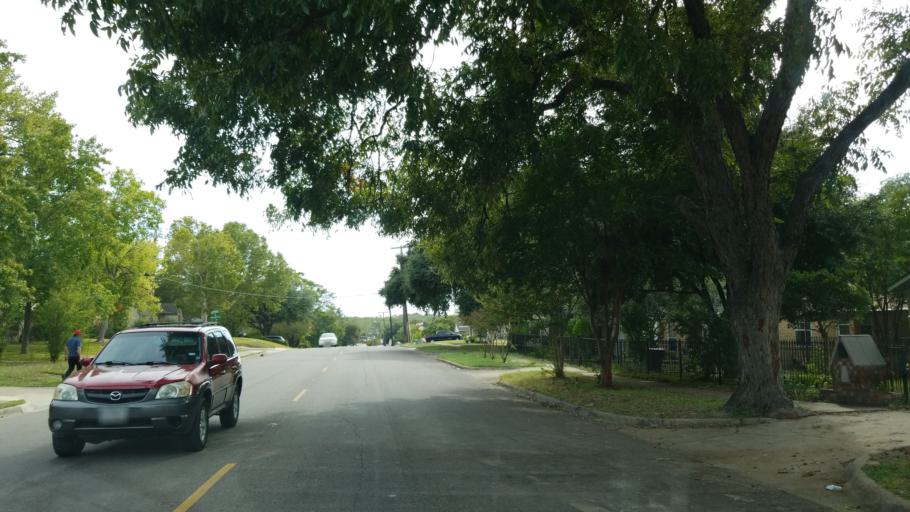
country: US
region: Texas
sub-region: Dallas County
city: Dallas
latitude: 32.7698
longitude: -96.7188
